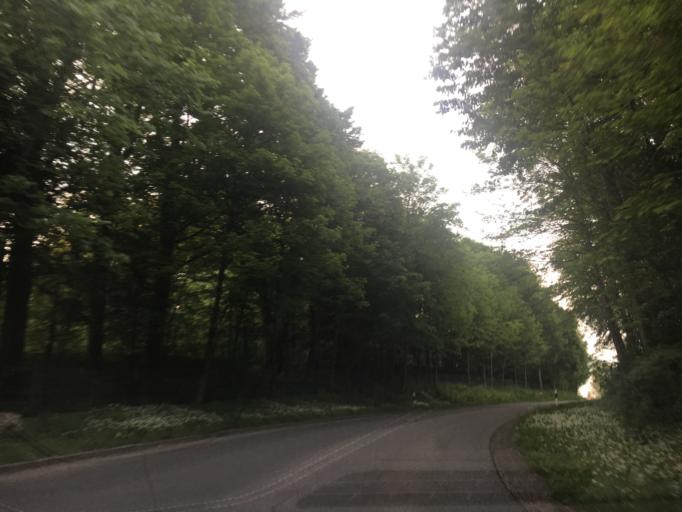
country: DE
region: Bavaria
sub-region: Upper Bavaria
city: Kochel
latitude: 47.6506
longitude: 11.3615
